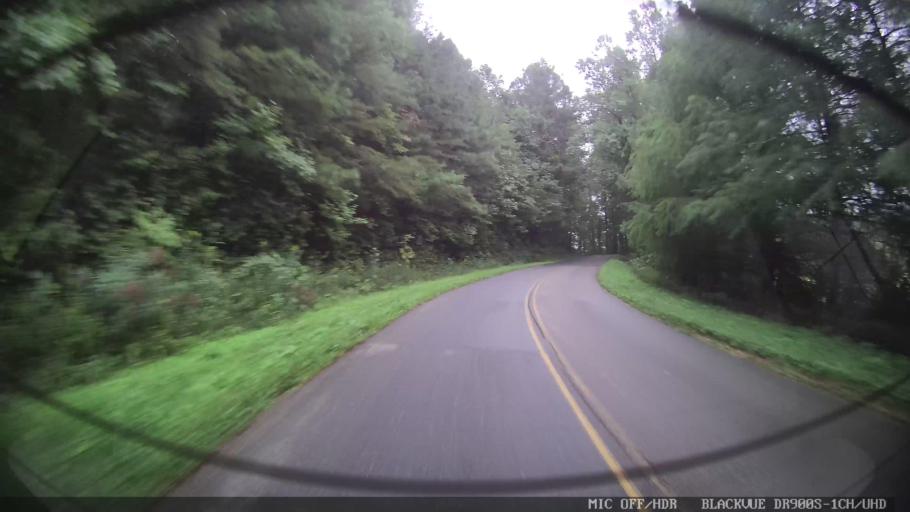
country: US
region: Georgia
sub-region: Gilmer County
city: Ellijay
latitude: 34.7733
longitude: -84.5363
